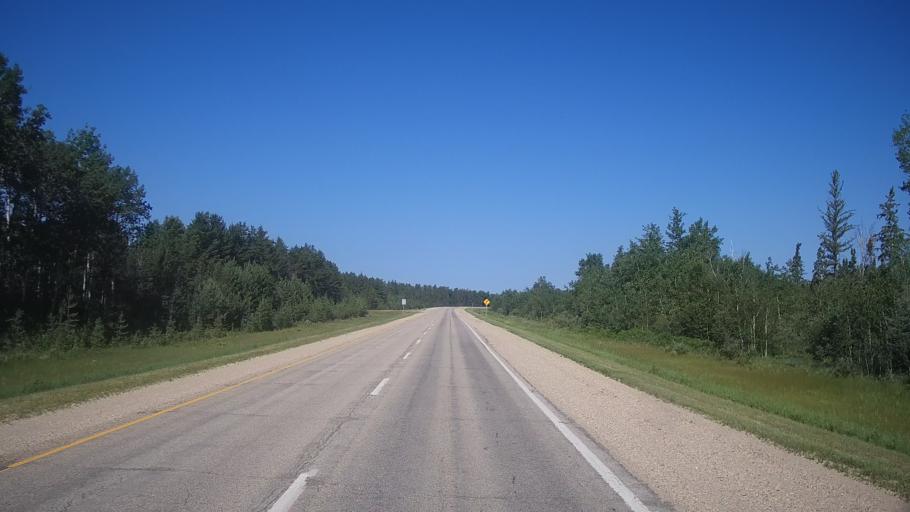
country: CA
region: Manitoba
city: La Broquerie
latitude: 49.6494
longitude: -95.9660
